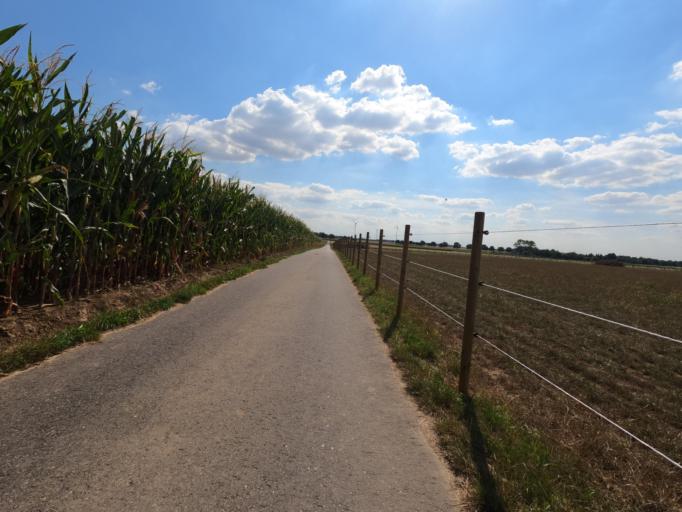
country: DE
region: North Rhine-Westphalia
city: Erkelenz
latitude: 51.0890
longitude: 6.2663
